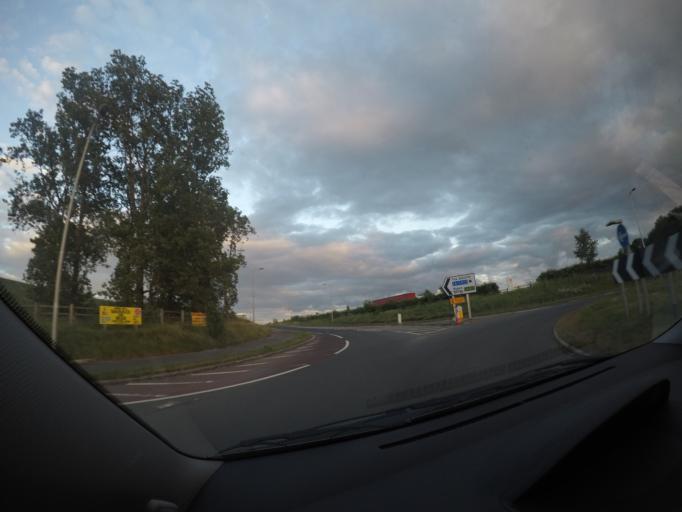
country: GB
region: England
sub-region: North Yorkshire
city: Ripon
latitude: 54.2236
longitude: -1.4884
